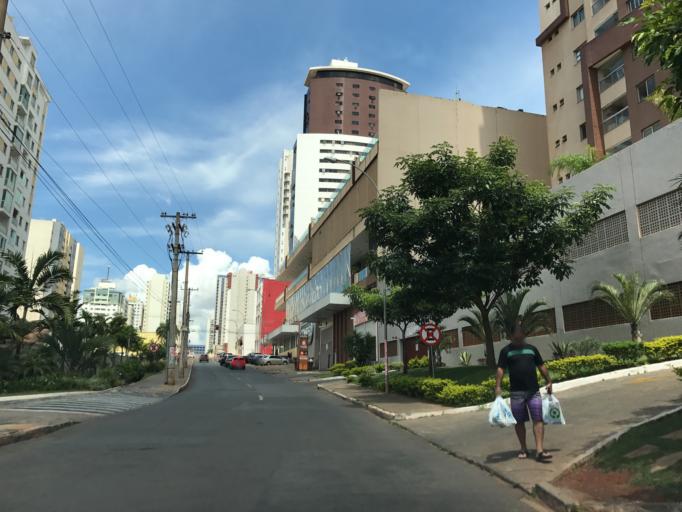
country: BR
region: Federal District
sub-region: Brasilia
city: Brasilia
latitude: -15.8334
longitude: -48.0362
